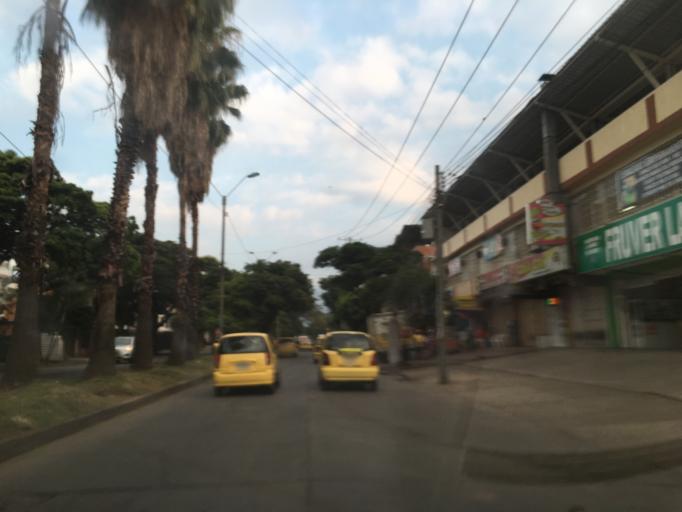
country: CO
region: Valle del Cauca
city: Cali
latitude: 3.4020
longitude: -76.5256
